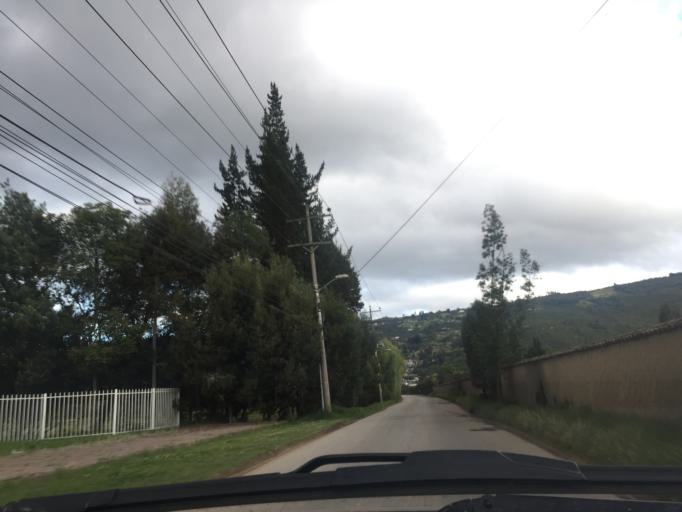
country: CO
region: Cundinamarca
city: Sopo
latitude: 4.9372
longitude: -73.9446
